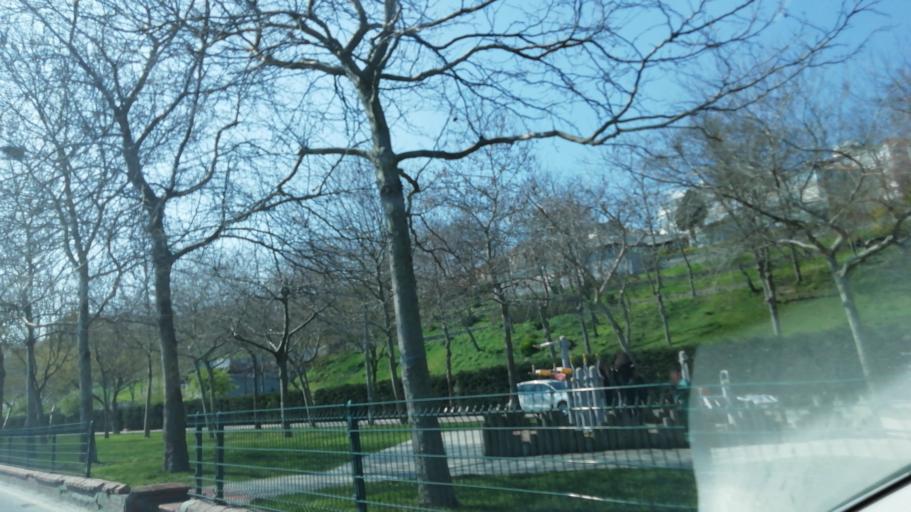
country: TR
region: Istanbul
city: Yakuplu
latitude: 40.9760
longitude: 28.7449
